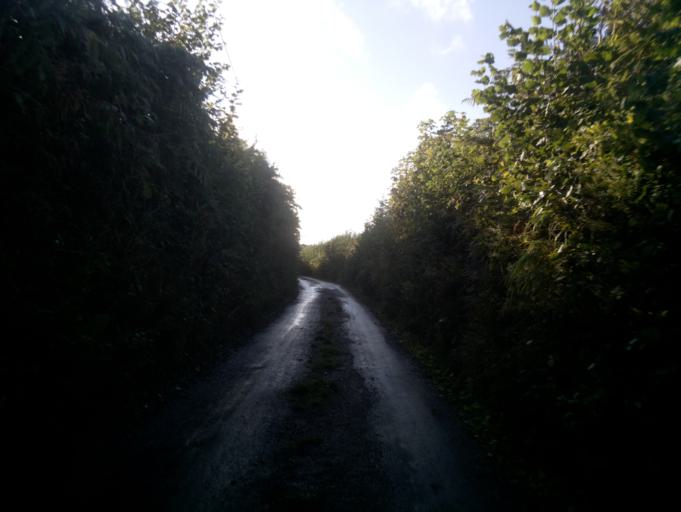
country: GB
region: England
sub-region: Devon
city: Totnes
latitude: 50.3460
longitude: -3.6984
